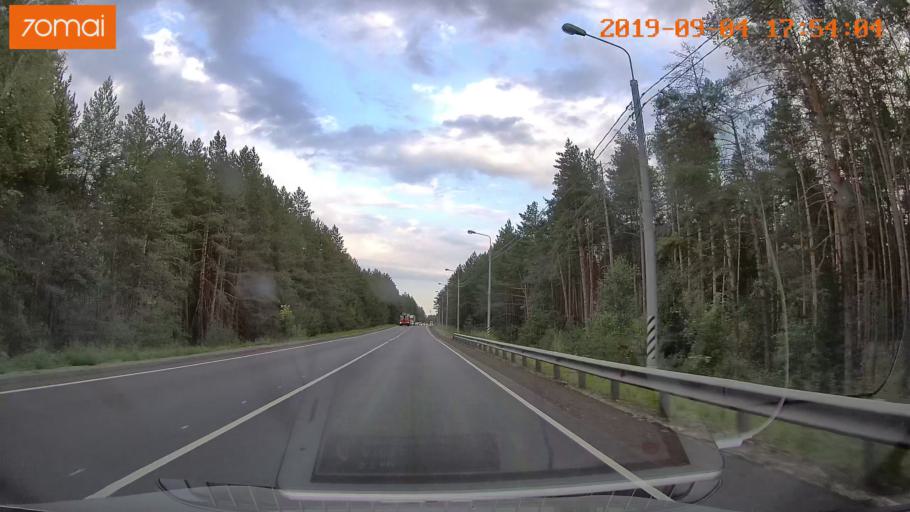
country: RU
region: Moskovskaya
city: Imeni Tsyurupy
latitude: 55.5127
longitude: 38.7354
